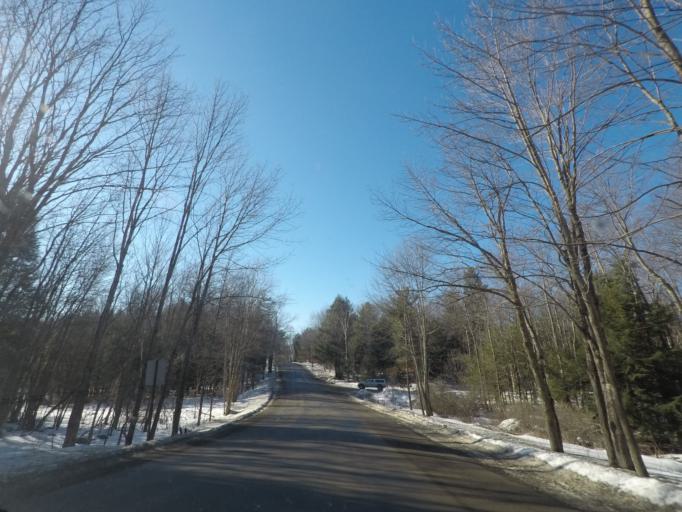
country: US
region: New York
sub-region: Rensselaer County
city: Averill Park
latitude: 42.6266
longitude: -73.5017
